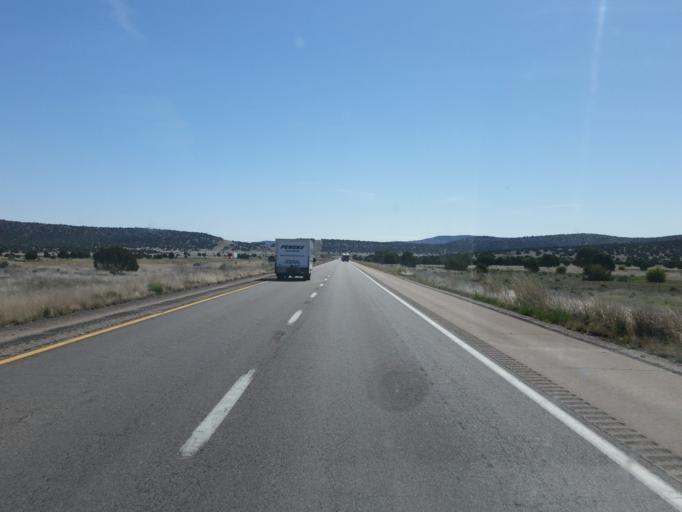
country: US
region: Arizona
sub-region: Mohave County
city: Peach Springs
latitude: 35.2276
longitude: -113.2302
